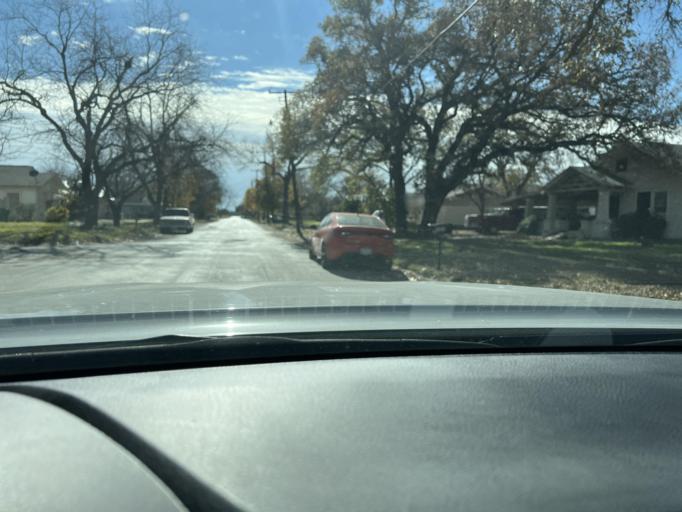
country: US
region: Texas
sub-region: Eastland County
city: Eastland
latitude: 32.3969
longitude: -98.8216
